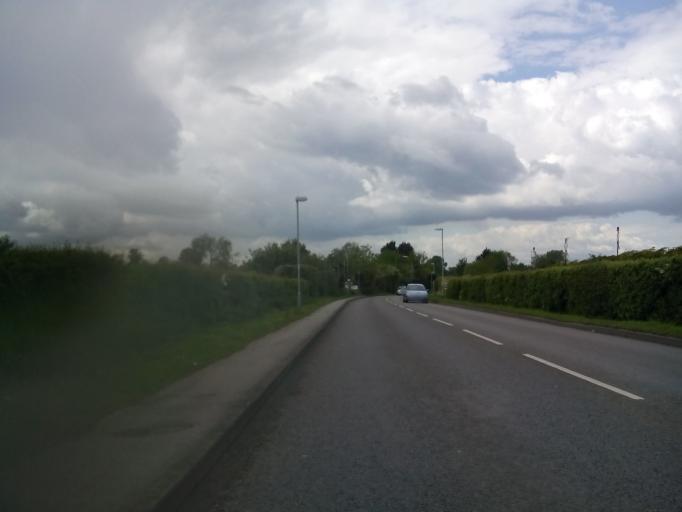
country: GB
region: England
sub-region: Cambridgeshire
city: Cambridge
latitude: 52.1986
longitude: 0.1633
